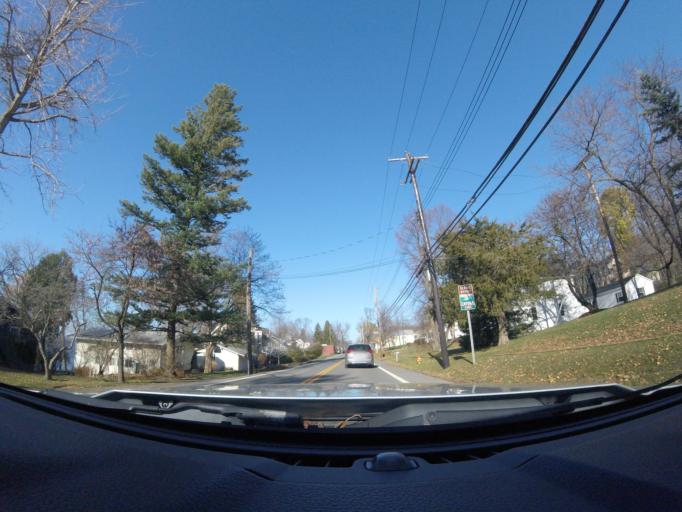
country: US
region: New York
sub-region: Cayuga County
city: Union Springs
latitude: 42.7480
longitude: -76.7005
